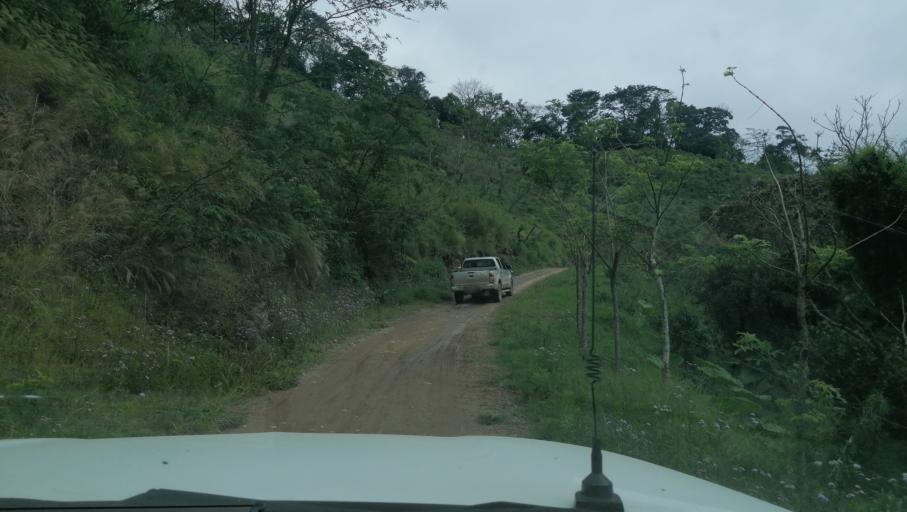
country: MX
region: Chiapas
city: Ostuacan
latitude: 17.3475
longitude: -93.3088
